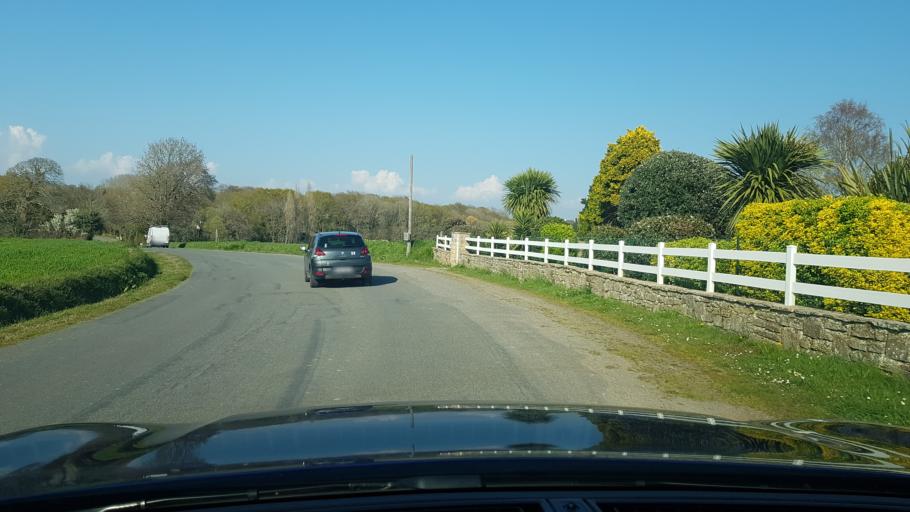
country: FR
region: Brittany
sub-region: Departement du Finistere
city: Moelan-sur-Mer
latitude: 47.7860
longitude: -3.6259
